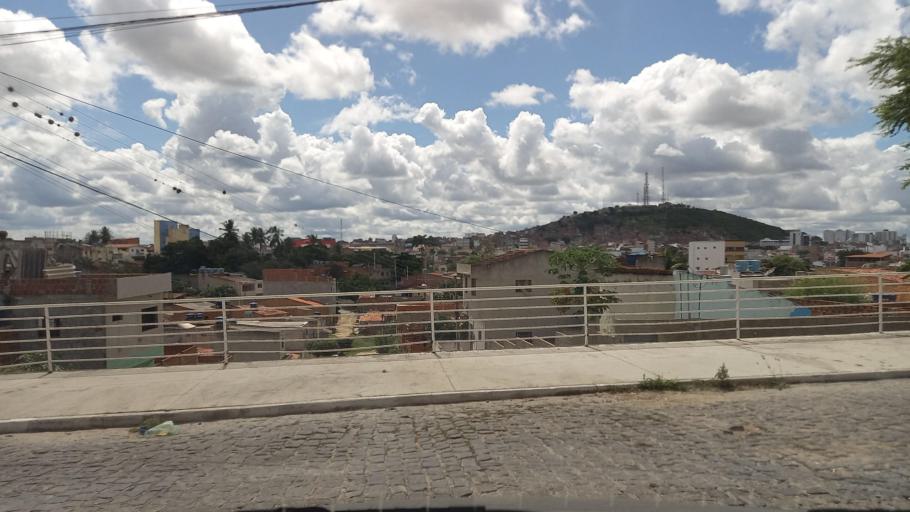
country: BR
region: Pernambuco
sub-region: Caruaru
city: Caruaru
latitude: -8.2974
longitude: -35.9803
